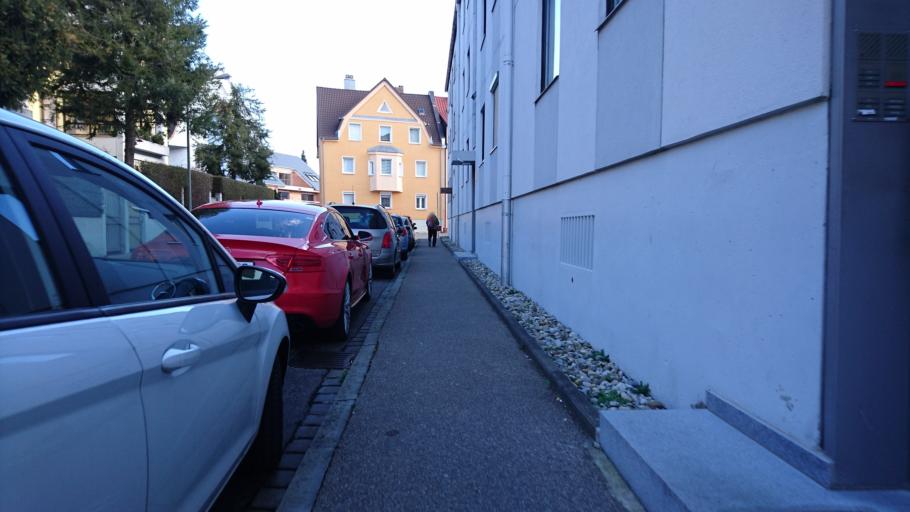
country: DE
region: Bavaria
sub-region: Swabia
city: Augsburg
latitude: 48.3820
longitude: 10.9128
